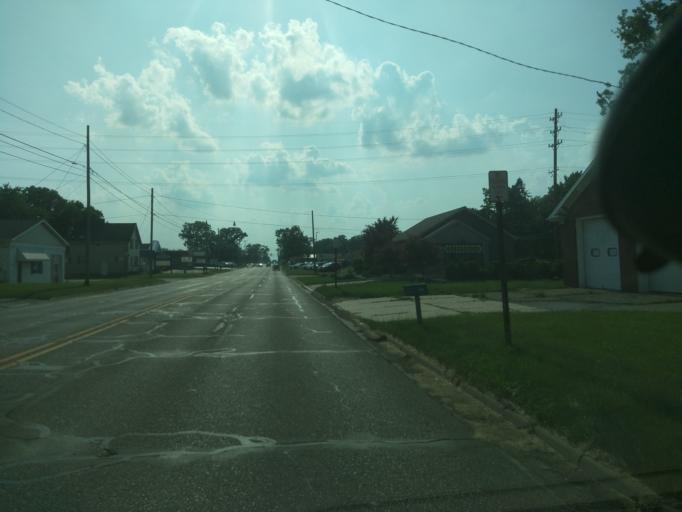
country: US
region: Michigan
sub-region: Jackson County
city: Jackson
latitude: 42.2548
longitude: -84.4444
